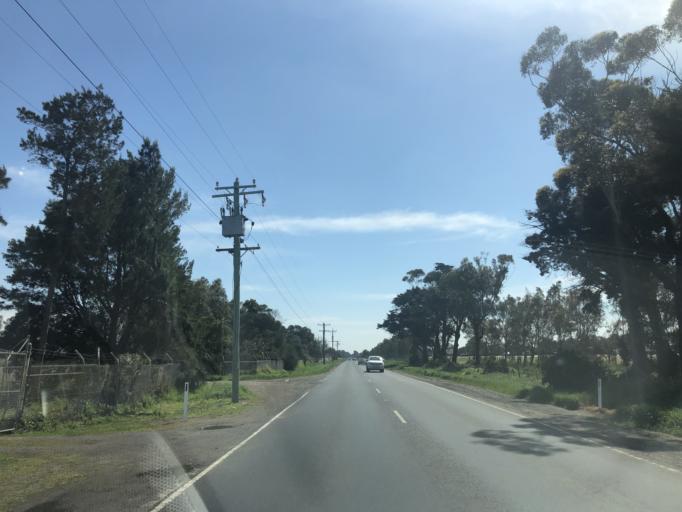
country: AU
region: Victoria
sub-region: Frankston
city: Sandhurst
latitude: -38.0529
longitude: 145.1844
